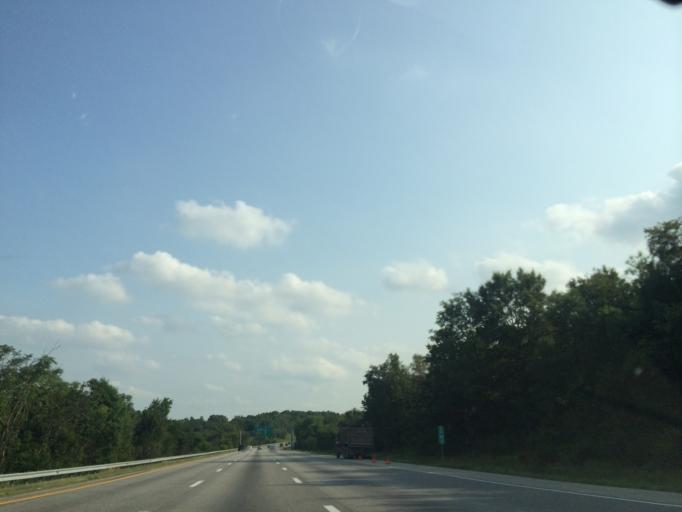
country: US
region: Pennsylvania
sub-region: Cumberland County
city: Enola
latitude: 40.2850
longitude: -76.9831
